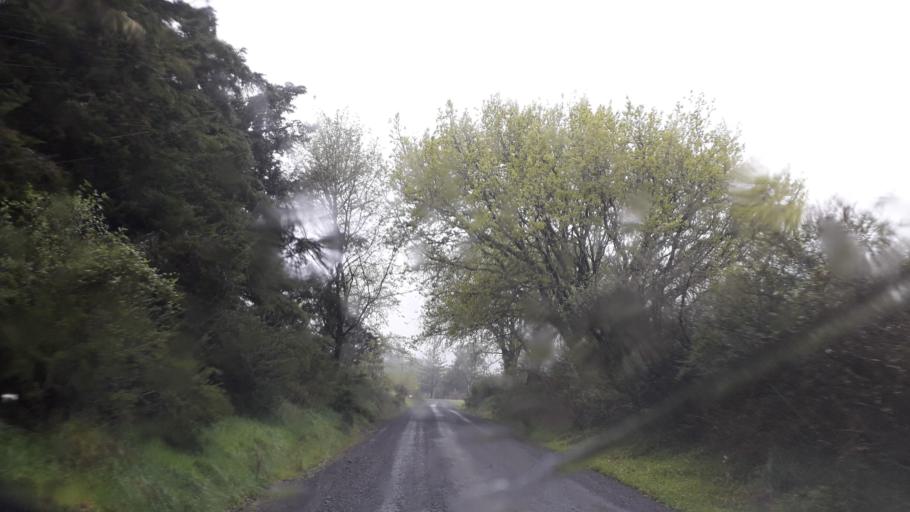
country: NZ
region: Northland
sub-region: Far North District
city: Waimate North
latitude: -35.4813
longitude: 173.6981
